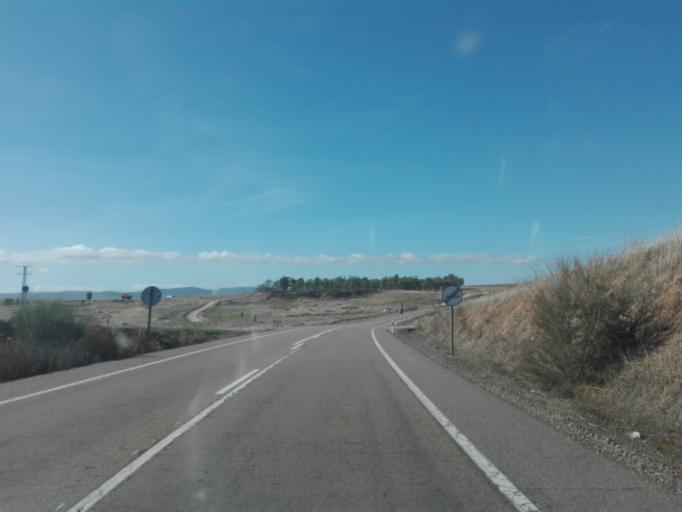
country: ES
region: Extremadura
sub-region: Provincia de Badajoz
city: Ahillones
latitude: 38.2604
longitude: -5.8707
